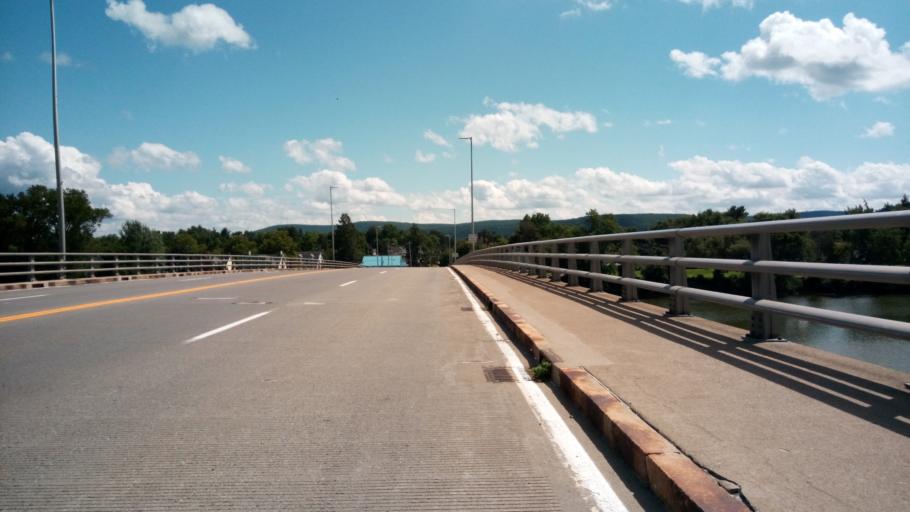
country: US
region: New York
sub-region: Chemung County
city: Elmira
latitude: 42.0836
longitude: -76.8156
